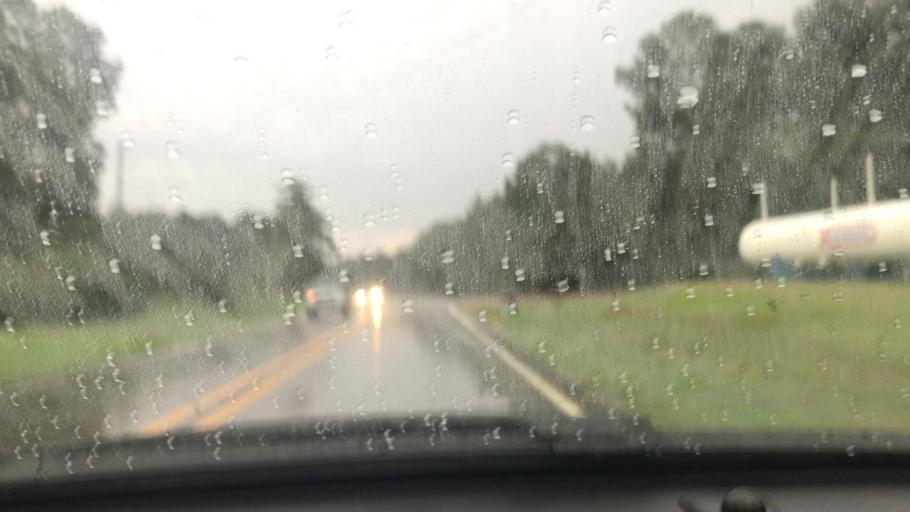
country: US
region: Mississippi
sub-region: Pike County
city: Summit
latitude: 31.3345
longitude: -90.5636
